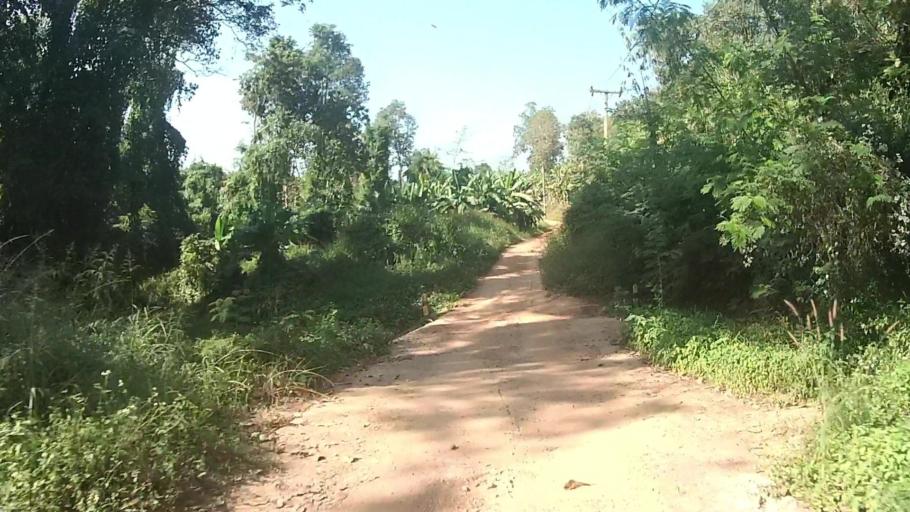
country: TH
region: Chiang Mai
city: Mae On
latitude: 18.9260
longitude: 99.1916
